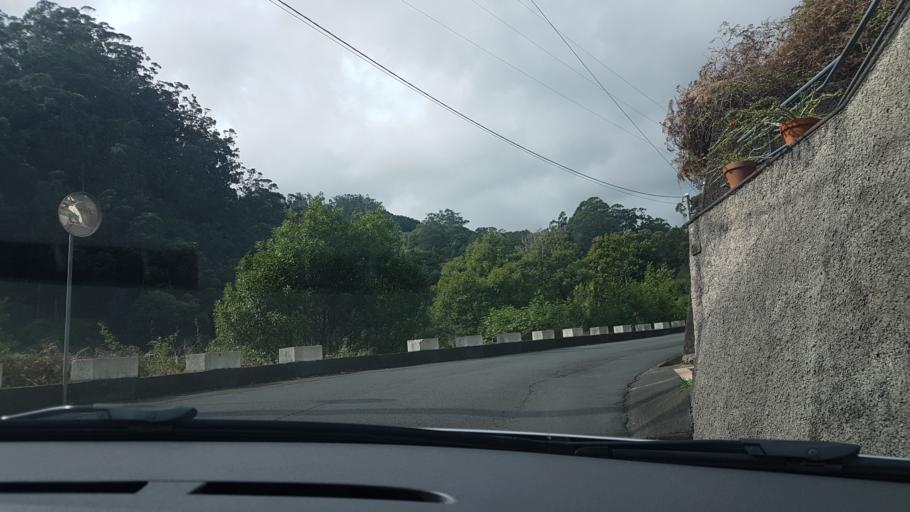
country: PT
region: Madeira
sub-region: Santa Cruz
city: Santa Cruz
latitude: 32.7357
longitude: -16.8089
